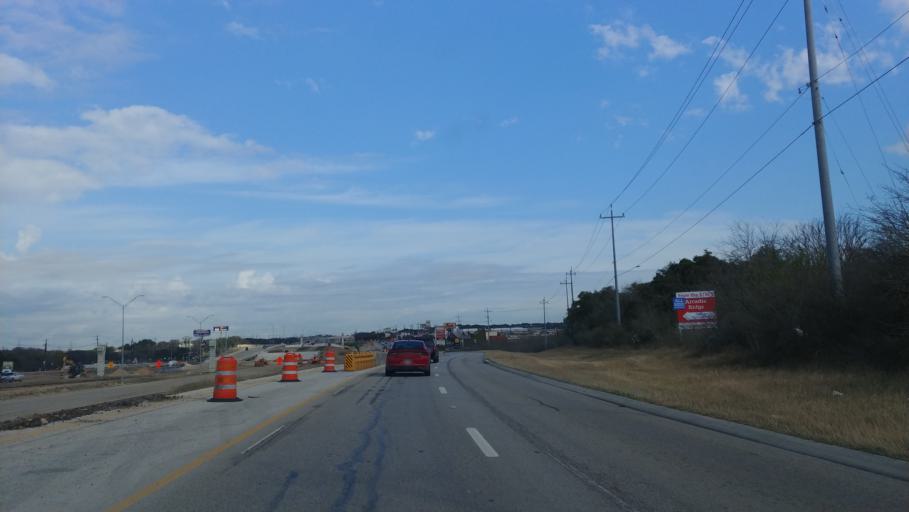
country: US
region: Texas
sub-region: Bexar County
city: Lackland Air Force Base
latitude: 29.4303
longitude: -98.7110
